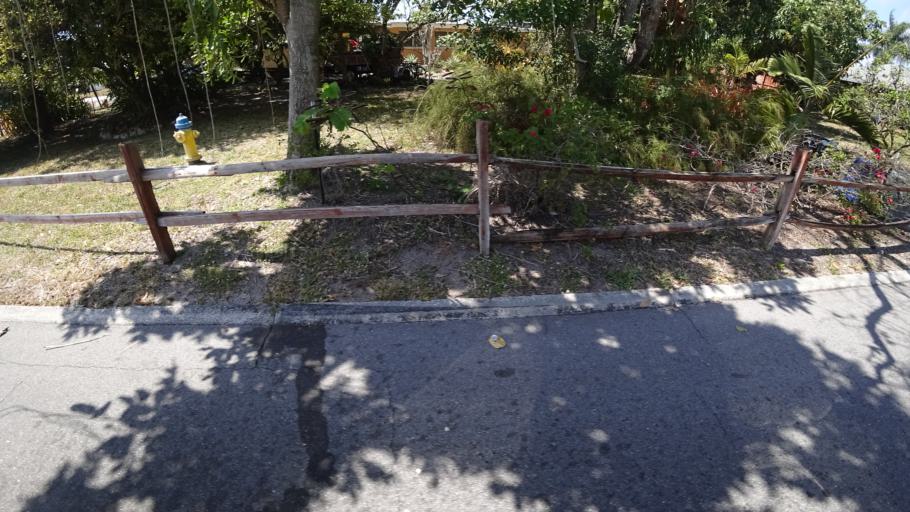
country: US
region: Florida
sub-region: Manatee County
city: Bayshore Gardens
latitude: 27.4271
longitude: -82.5809
